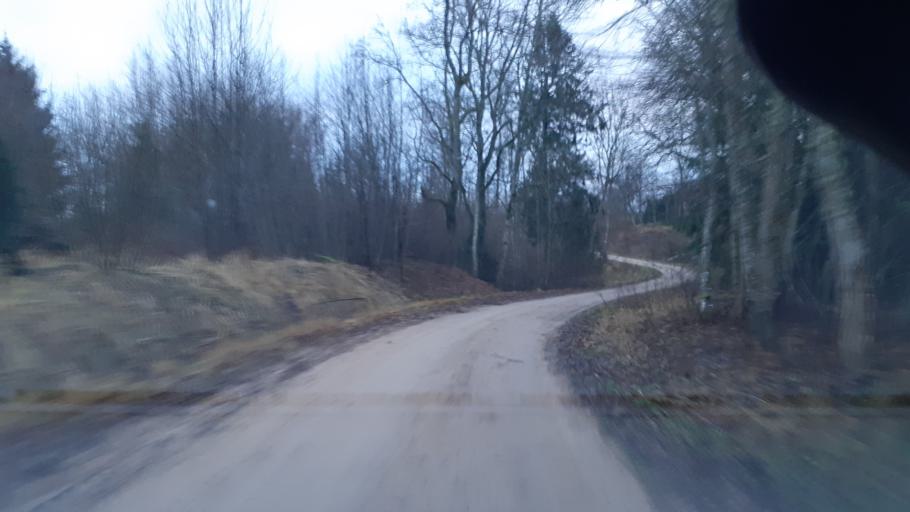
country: LV
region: Alsunga
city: Alsunga
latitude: 56.9147
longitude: 21.7141
